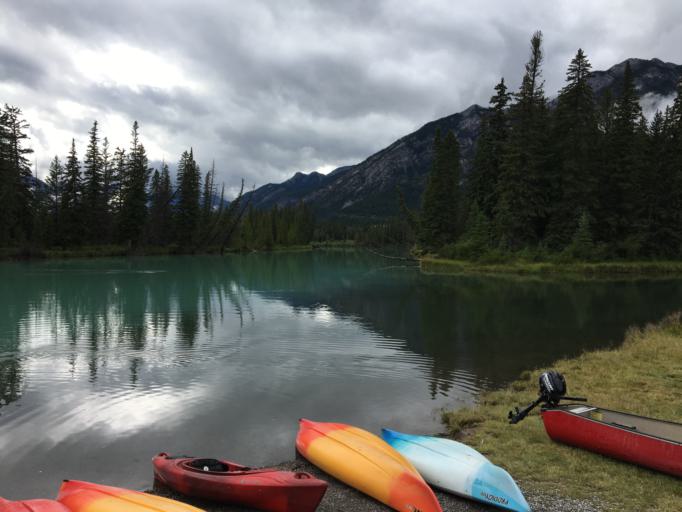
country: CA
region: Alberta
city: Banff
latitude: 51.1781
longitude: -115.5770
